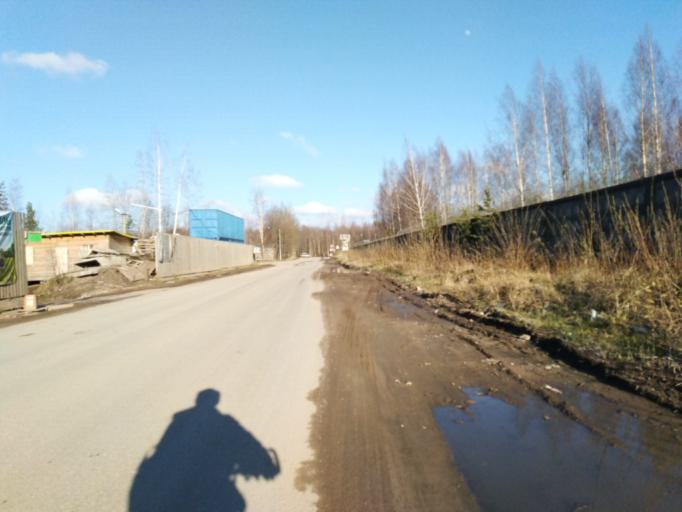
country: RU
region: Leningrad
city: Novoye Devyatkino
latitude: 60.0669
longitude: 30.4917
